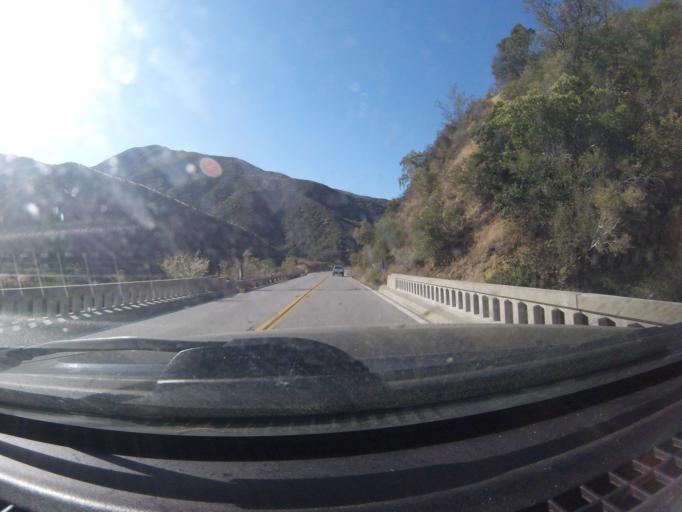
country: US
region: California
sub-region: San Bernardino County
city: Highland
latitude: 34.1733
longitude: -117.1823
